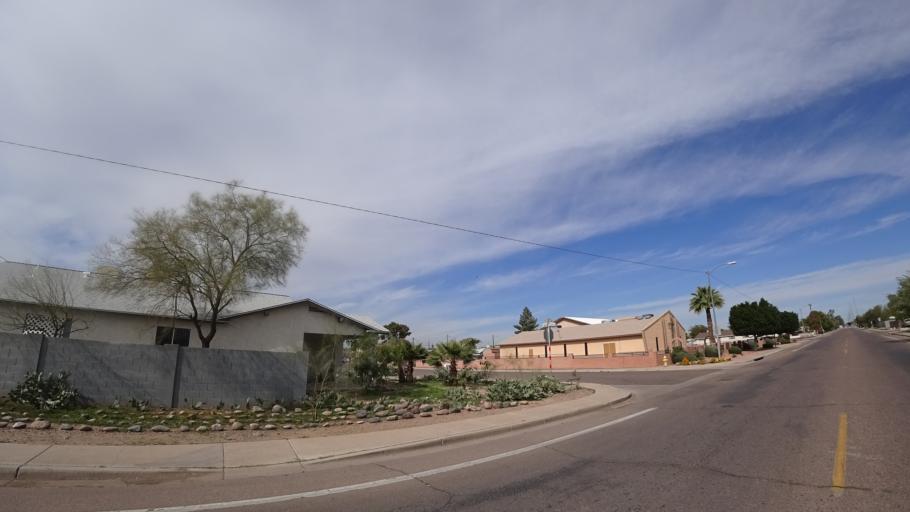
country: US
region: Arizona
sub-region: Maricopa County
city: Phoenix
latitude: 33.4686
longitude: -112.1258
